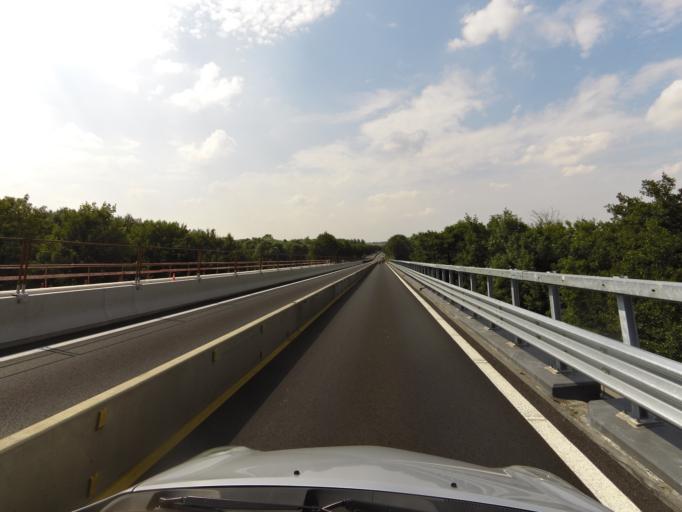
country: FR
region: Picardie
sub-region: Departement de l'Aisne
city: Itancourt
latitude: 49.7539
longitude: 3.3789
